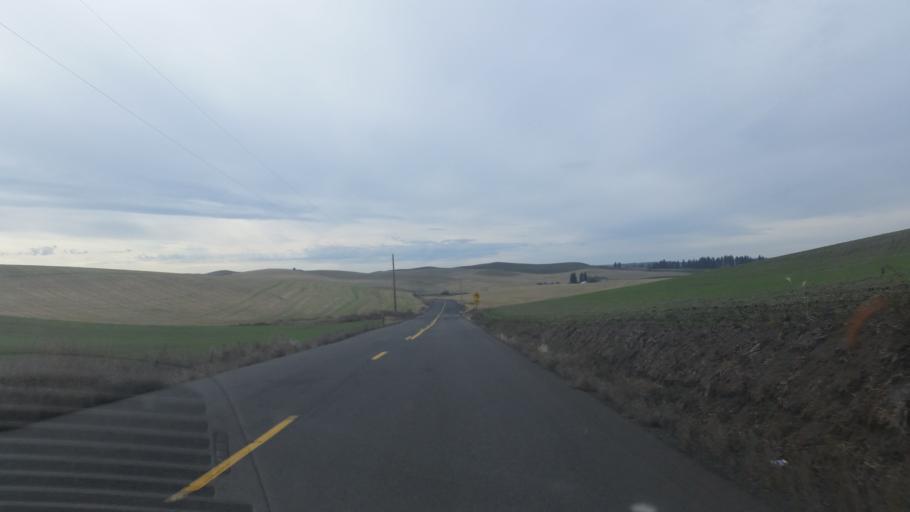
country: US
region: Washington
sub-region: Spokane County
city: Cheney
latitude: 47.3114
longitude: -117.4889
